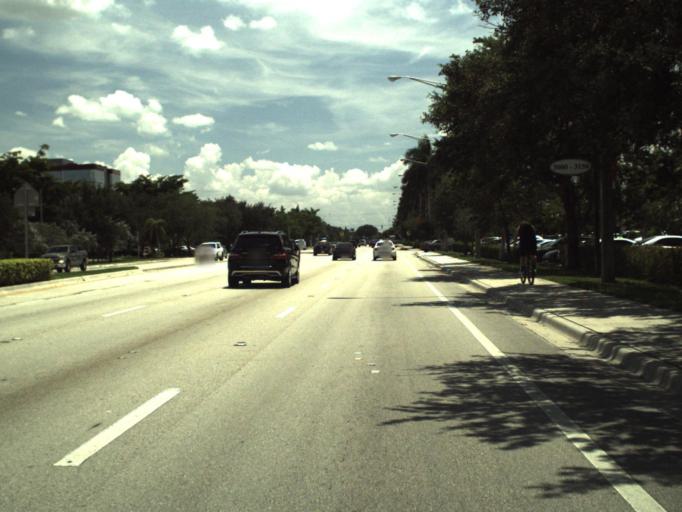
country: US
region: Florida
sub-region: Broward County
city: Coral Springs
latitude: 26.2684
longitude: -80.2502
